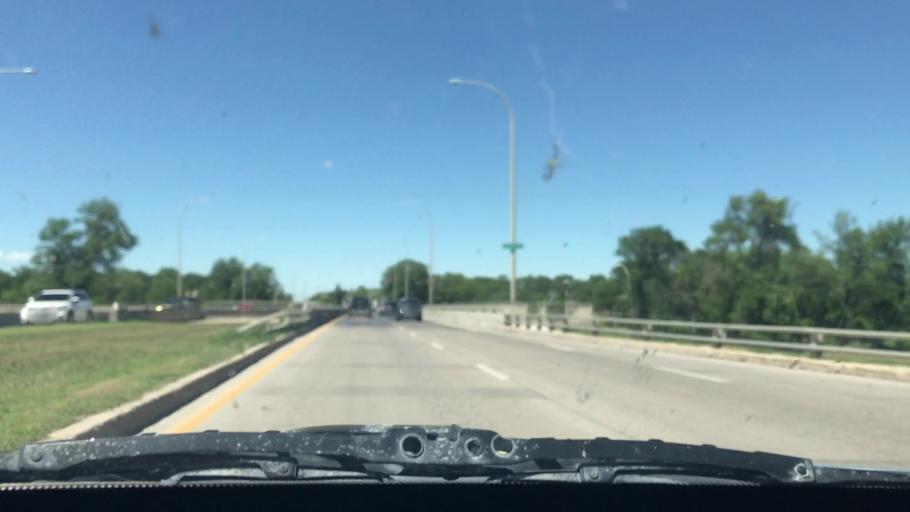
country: CA
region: Manitoba
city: Winnipeg
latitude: 49.8541
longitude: -97.1256
